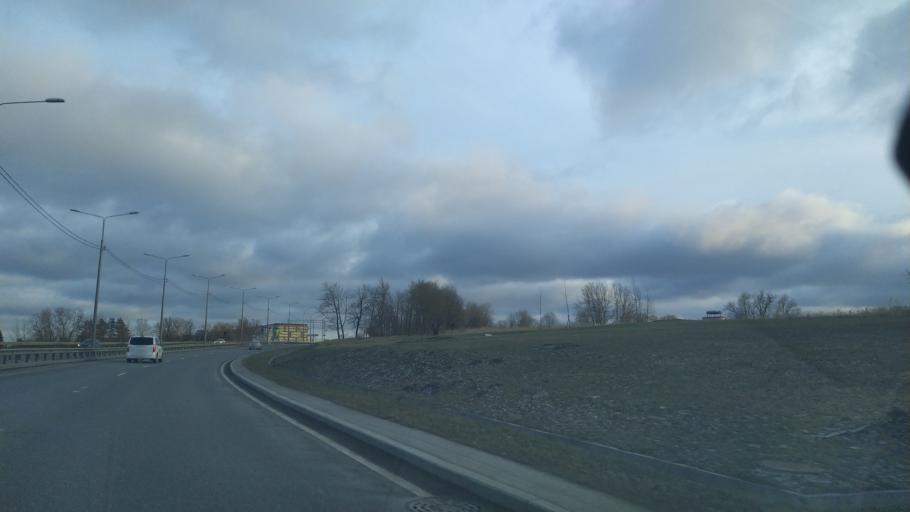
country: RU
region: St.-Petersburg
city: Aleksandrovskaya
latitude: 59.7713
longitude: 30.3425
